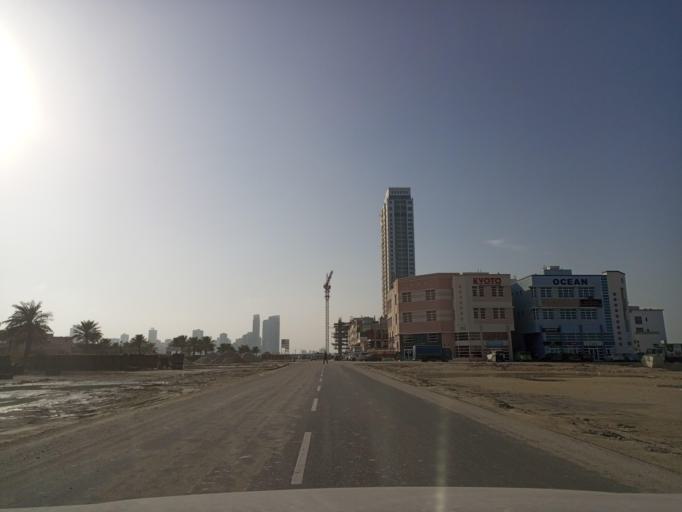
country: BH
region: Muharraq
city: Al Hadd
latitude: 26.2260
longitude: 50.6341
